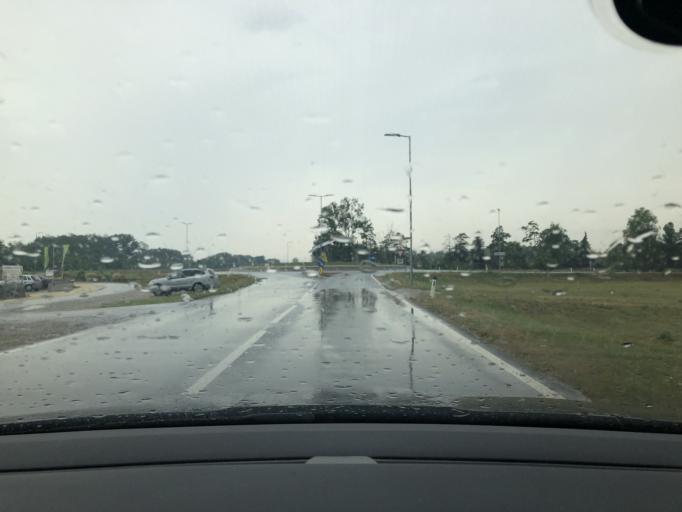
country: AT
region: Lower Austria
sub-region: Politischer Bezirk Ganserndorf
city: Weikendorf
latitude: 48.3412
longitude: 16.7569
